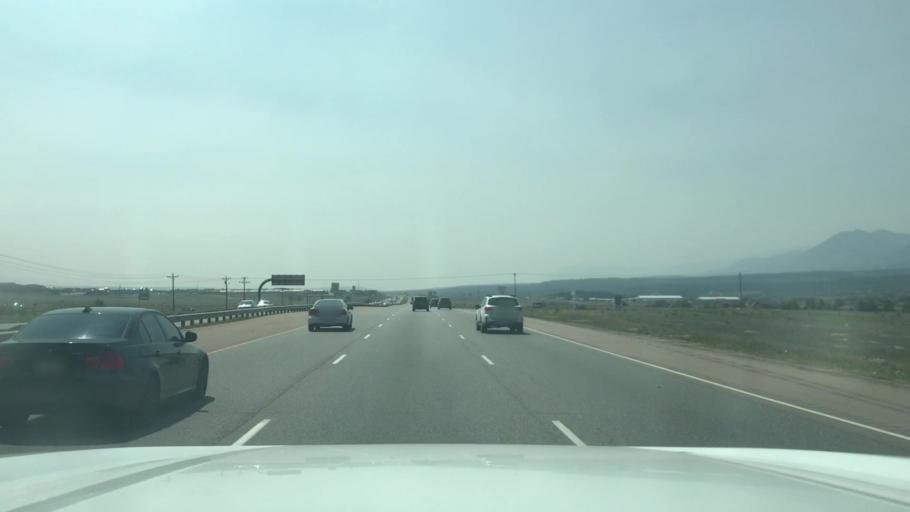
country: US
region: Colorado
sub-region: El Paso County
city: Monument
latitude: 39.0806
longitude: -104.8601
